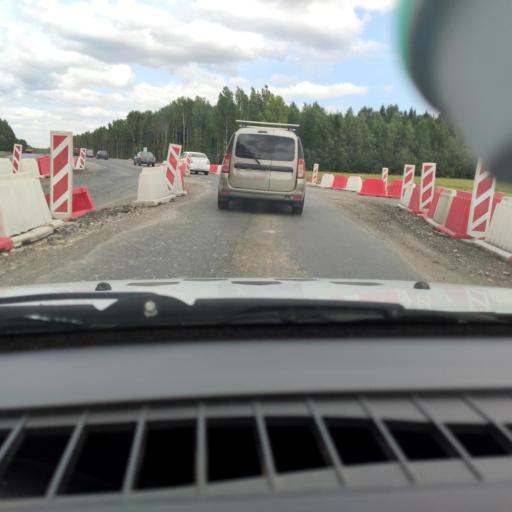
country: RU
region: Perm
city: Solikamsk
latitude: 59.5356
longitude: 56.8016
